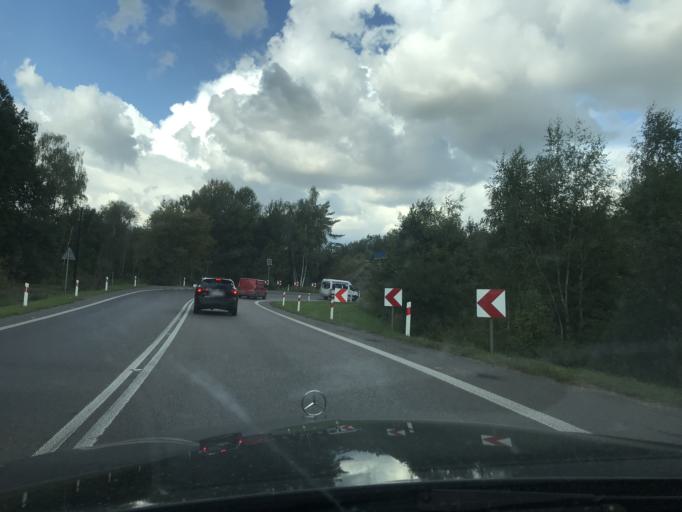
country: PL
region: Lublin Voivodeship
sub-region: Powiat lubelski
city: Niemce
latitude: 51.3856
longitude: 22.6354
